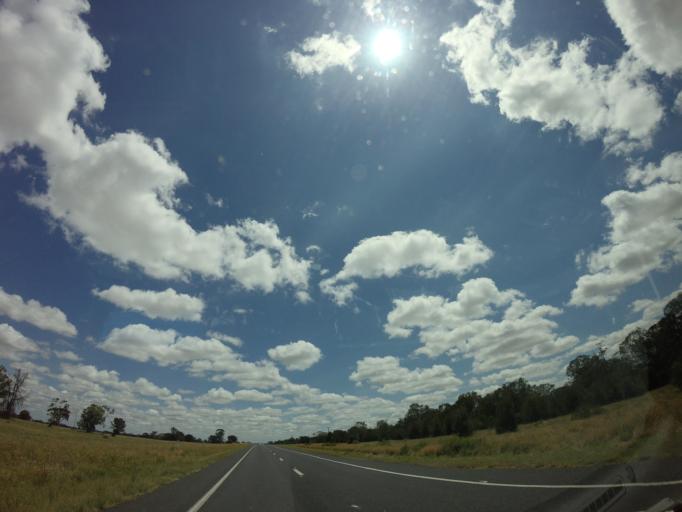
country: AU
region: New South Wales
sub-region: Moree Plains
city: Moree
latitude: -29.1296
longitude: 150.0247
